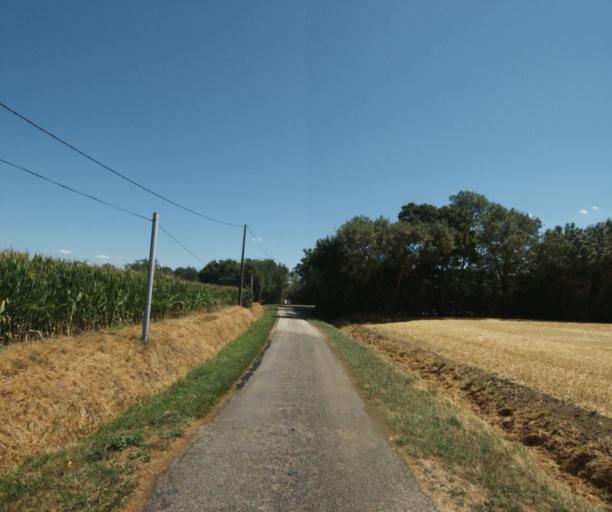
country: FR
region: Midi-Pyrenees
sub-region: Departement de la Haute-Garonne
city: Revel
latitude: 43.4742
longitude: 1.9514
